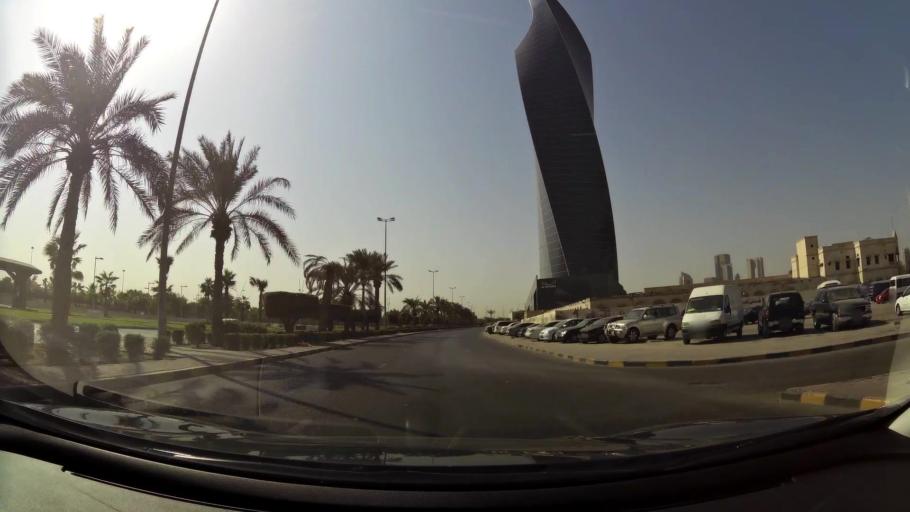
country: KW
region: Al Asimah
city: Ad Dasmah
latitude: 29.3721
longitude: 47.9937
